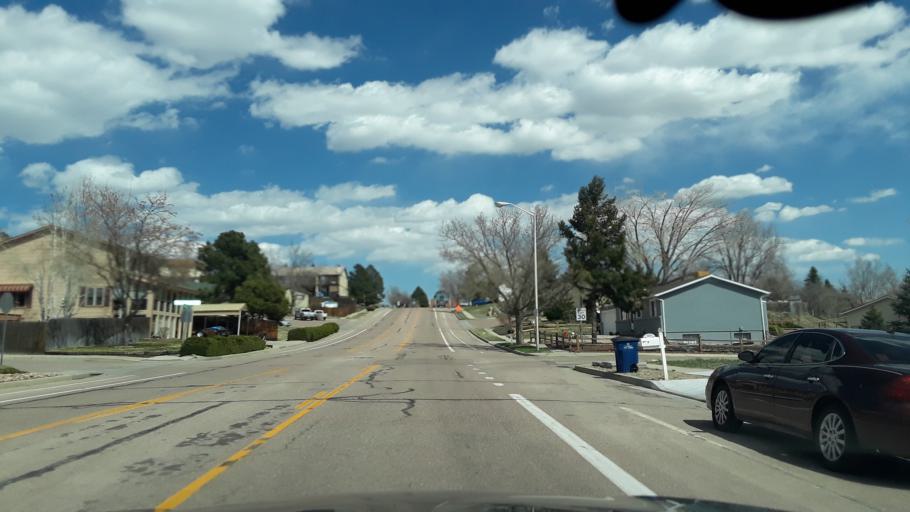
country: US
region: Colorado
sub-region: El Paso County
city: Colorado Springs
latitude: 38.9097
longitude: -104.7793
